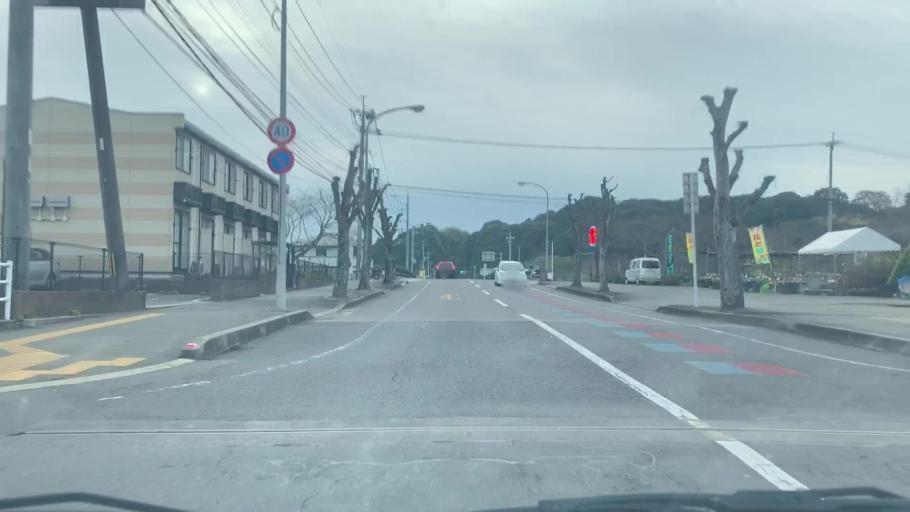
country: JP
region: Saga Prefecture
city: Takeocho-takeo
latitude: 33.1945
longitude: 130.0299
